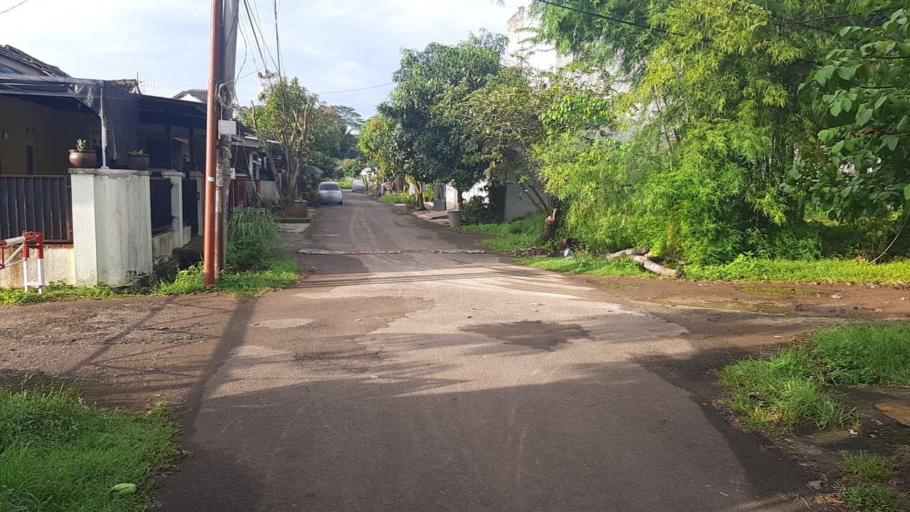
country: ID
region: West Java
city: Cileungsir
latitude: -6.3767
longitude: 107.0042
